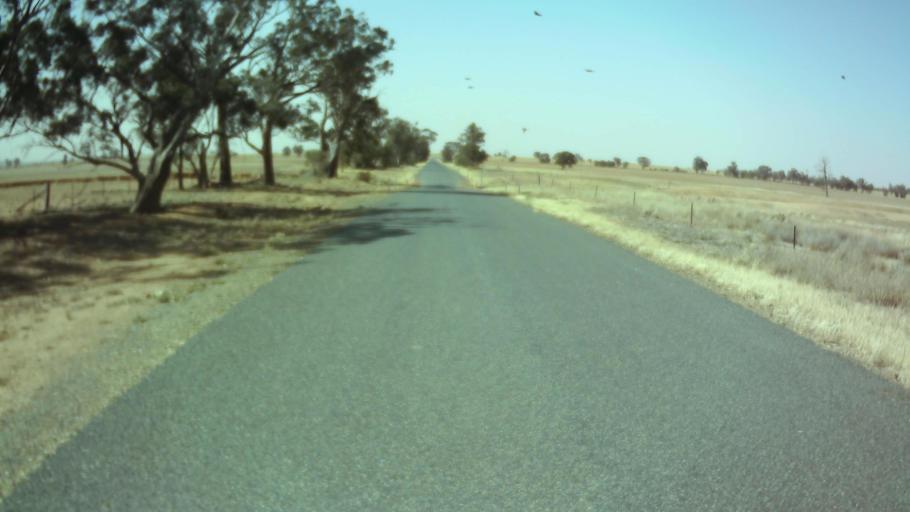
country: AU
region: New South Wales
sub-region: Weddin
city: Grenfell
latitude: -33.8677
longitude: 147.9270
